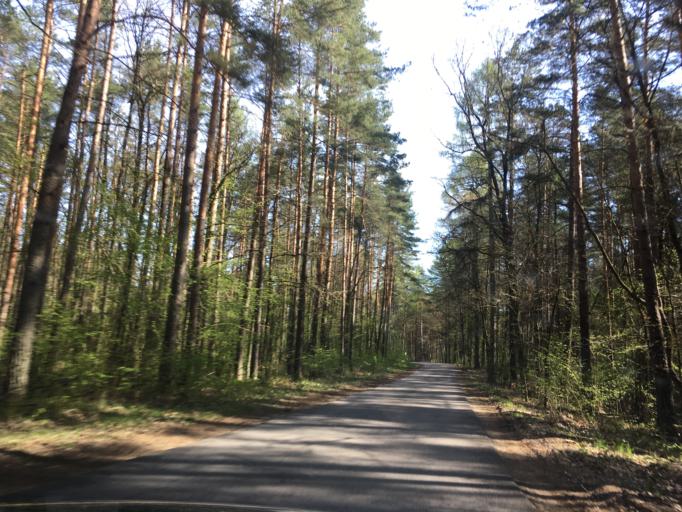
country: PL
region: Warmian-Masurian Voivodeship
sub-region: Powiat piski
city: Ruciane-Nida
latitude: 53.6792
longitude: 21.5879
